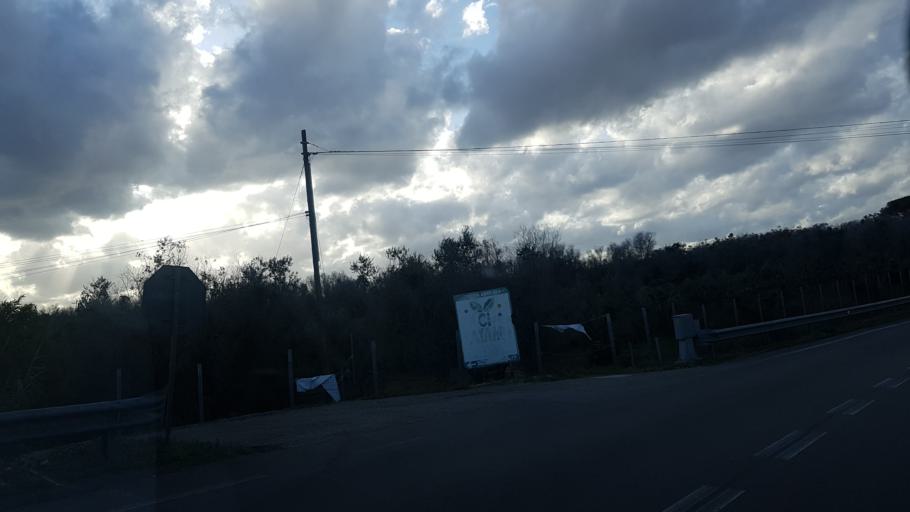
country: IT
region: Apulia
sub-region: Provincia di Brindisi
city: Torchiarolo
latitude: 40.4862
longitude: 18.0393
